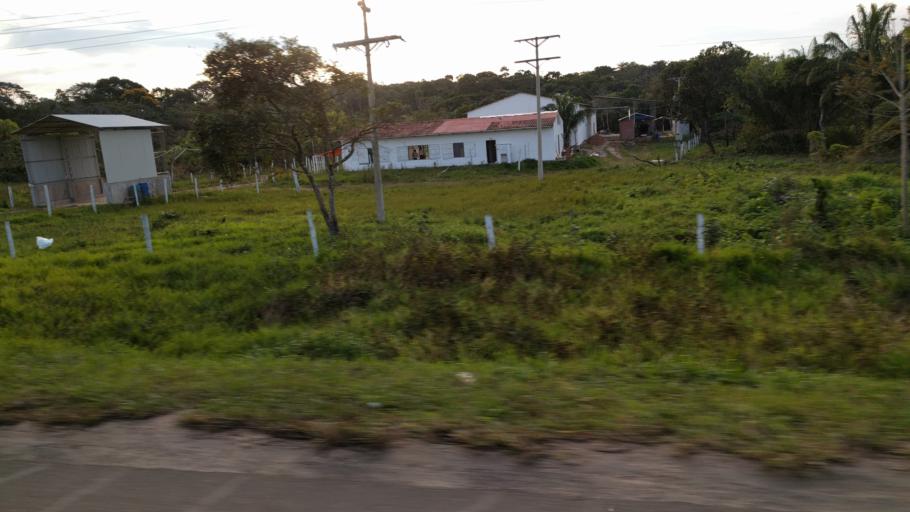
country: BO
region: Santa Cruz
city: Buena Vista
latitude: -17.4366
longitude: -63.6402
